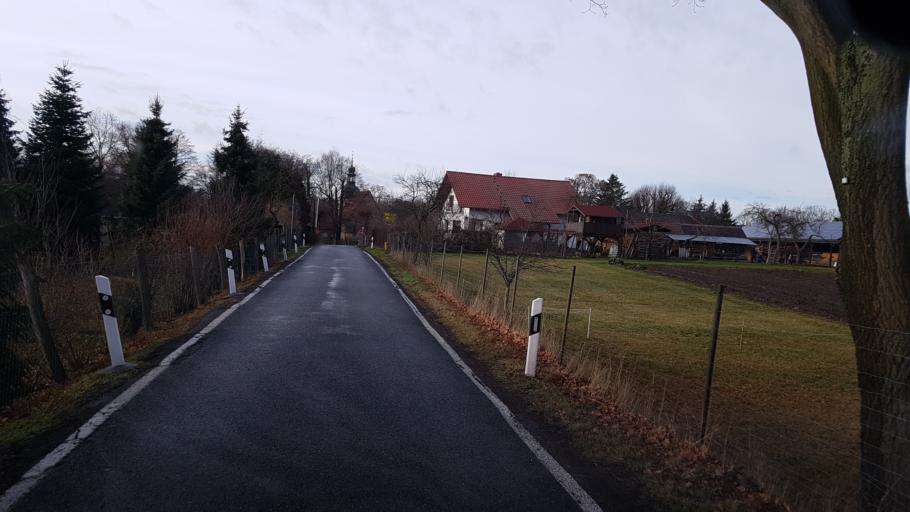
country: DE
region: Brandenburg
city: Bronkow
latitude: 51.6700
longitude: 13.9183
